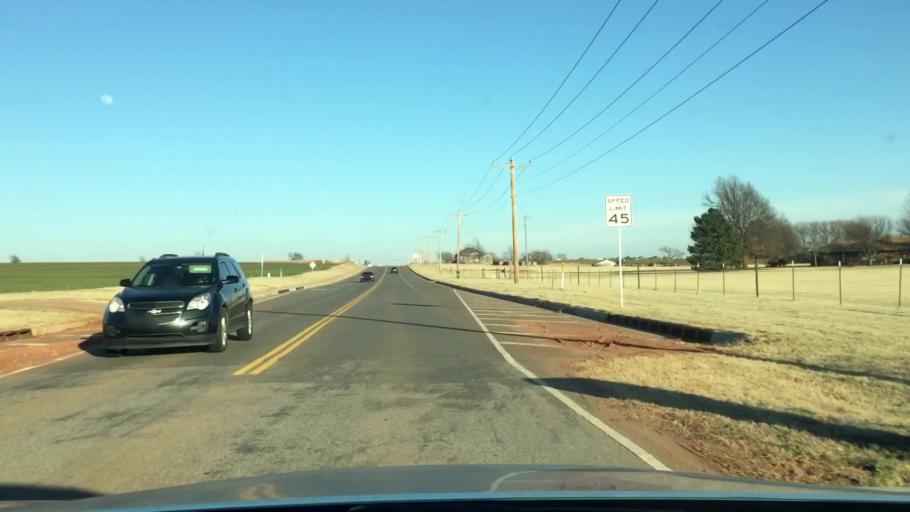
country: US
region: Oklahoma
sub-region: Oklahoma County
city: The Village
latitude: 35.6531
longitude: -97.5940
